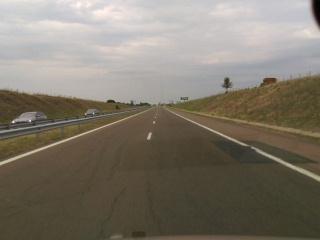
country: BG
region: Burgas
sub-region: Obshtina Karnobat
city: Karnobat
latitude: 42.5900
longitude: 27.0474
